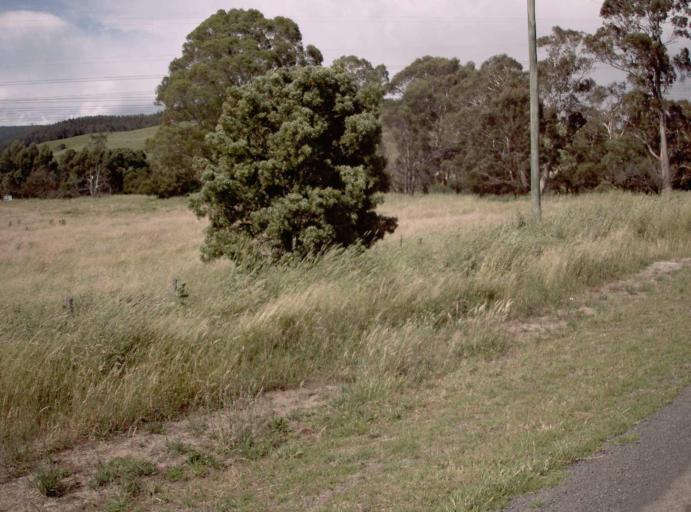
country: AU
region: Victoria
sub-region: Latrobe
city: Morwell
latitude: -38.1482
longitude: 146.4469
